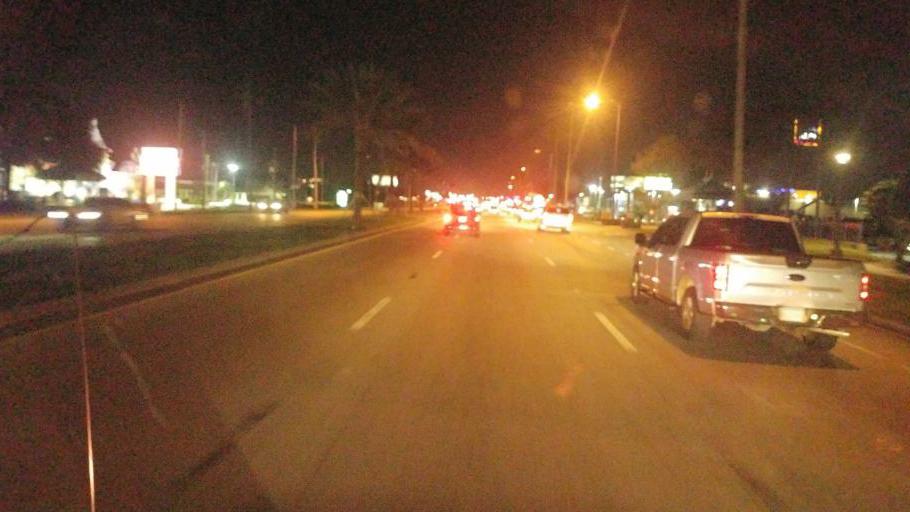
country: US
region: Florida
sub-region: Osceola County
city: Celebration
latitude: 28.3328
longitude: -81.4955
